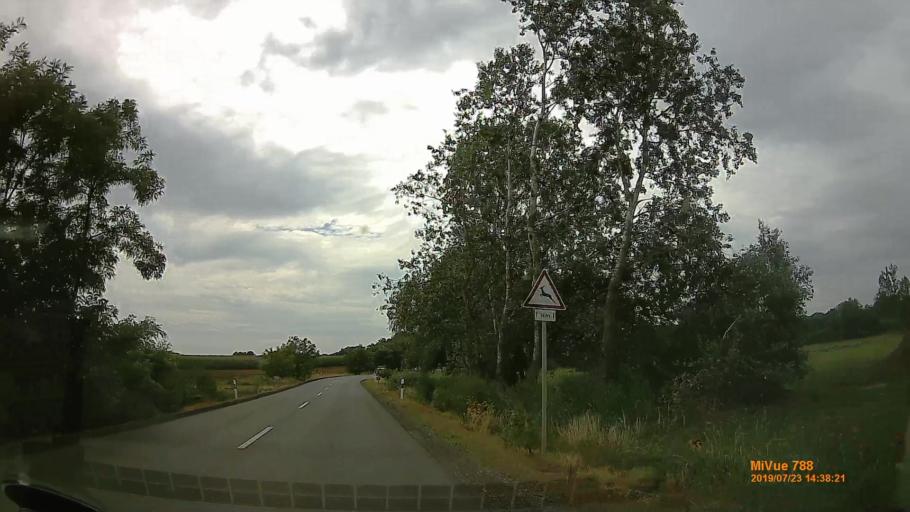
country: HU
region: Szabolcs-Szatmar-Bereg
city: Nyiregyhaza
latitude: 47.9264
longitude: 21.6685
